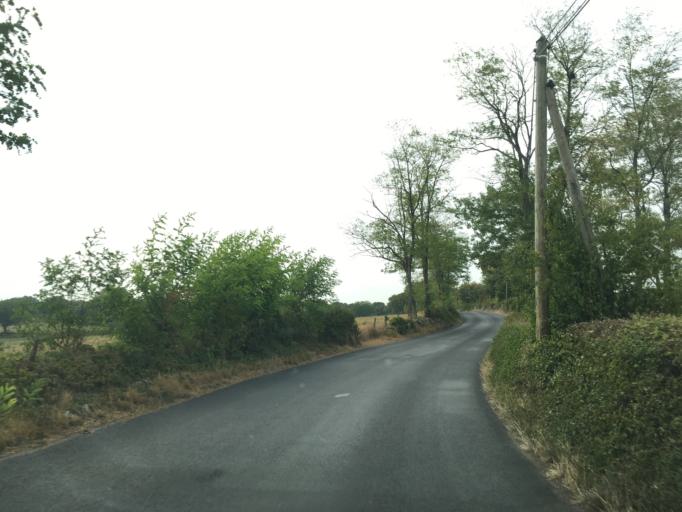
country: FR
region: Midi-Pyrenees
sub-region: Departement du Lot
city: Gramat
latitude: 44.8102
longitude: 1.6120
